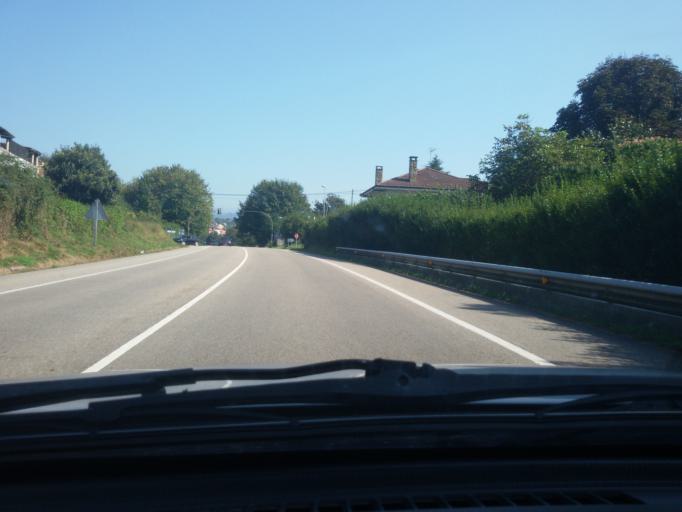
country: ES
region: Asturias
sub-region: Province of Asturias
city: Pola de Siero
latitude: 43.3879
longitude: -5.6762
